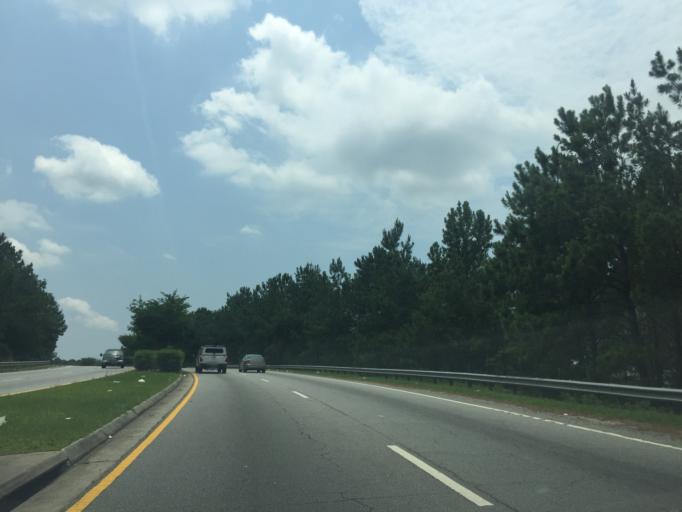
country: US
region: Georgia
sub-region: Chatham County
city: Garden City
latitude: 32.0452
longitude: -81.1662
